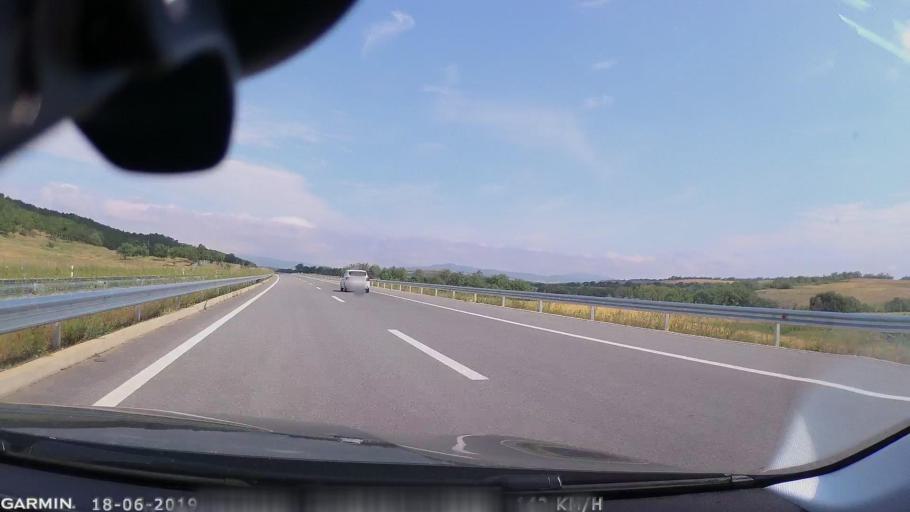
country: MK
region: Sveti Nikole
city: Sveti Nikole
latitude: 41.8922
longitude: 21.9269
